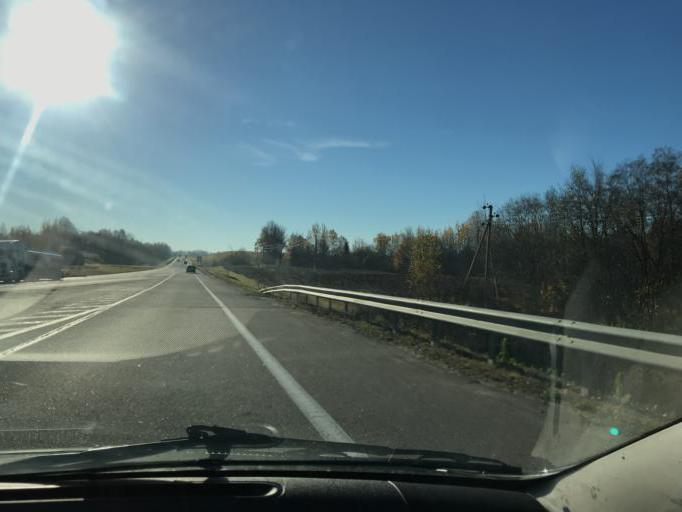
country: BY
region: Vitebsk
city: Vitebsk
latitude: 55.0979
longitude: 30.3000
